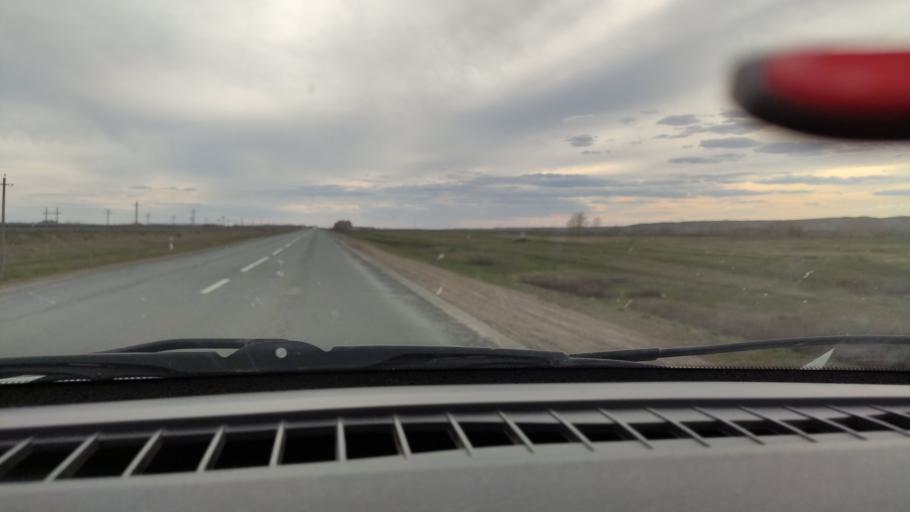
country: RU
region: Bashkortostan
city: Mayachnyy
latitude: 52.4162
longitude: 55.7630
